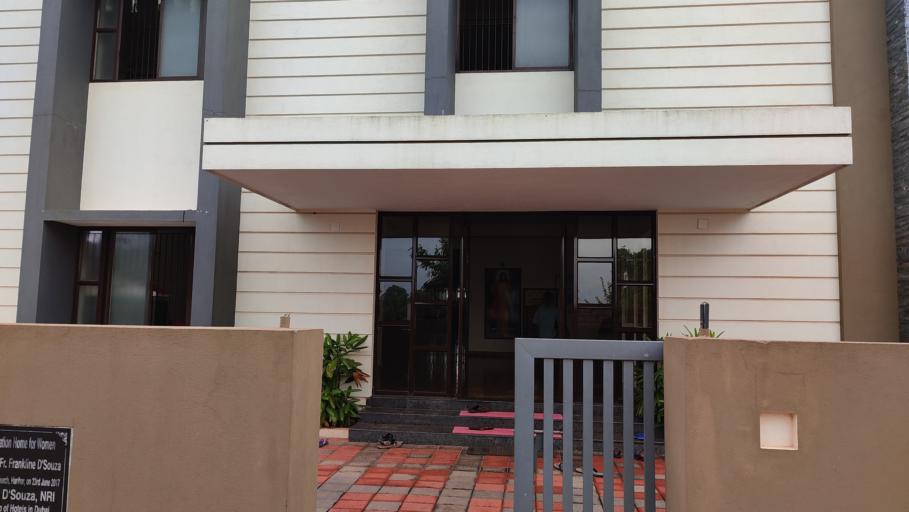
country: IN
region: Kerala
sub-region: Kasaragod District
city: Manjeshwara
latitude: 12.7523
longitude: 74.9023
